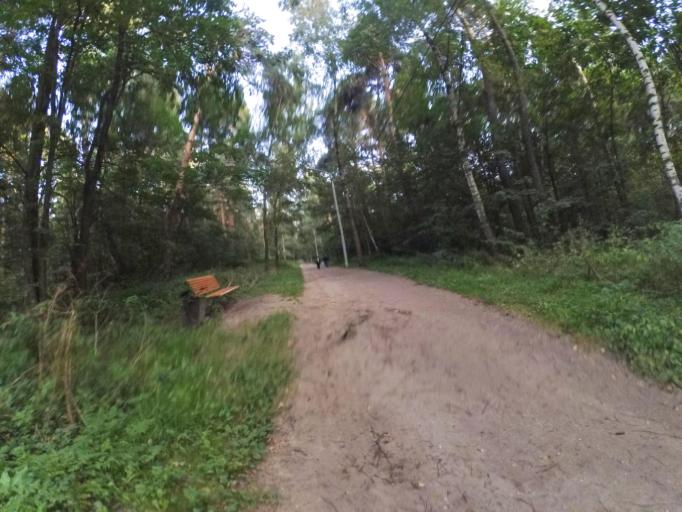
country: RU
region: Moscow
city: Kuz'minki
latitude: 55.6930
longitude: 37.7968
